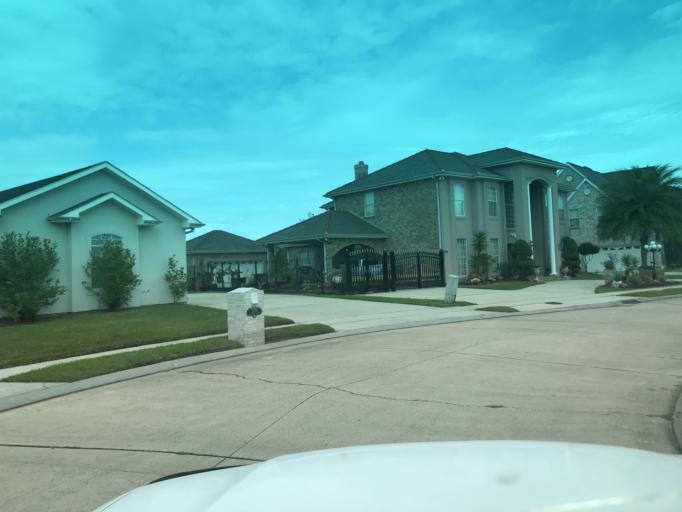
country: US
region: Louisiana
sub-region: Saint Bernard Parish
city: Chalmette
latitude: 30.0357
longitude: -89.9494
